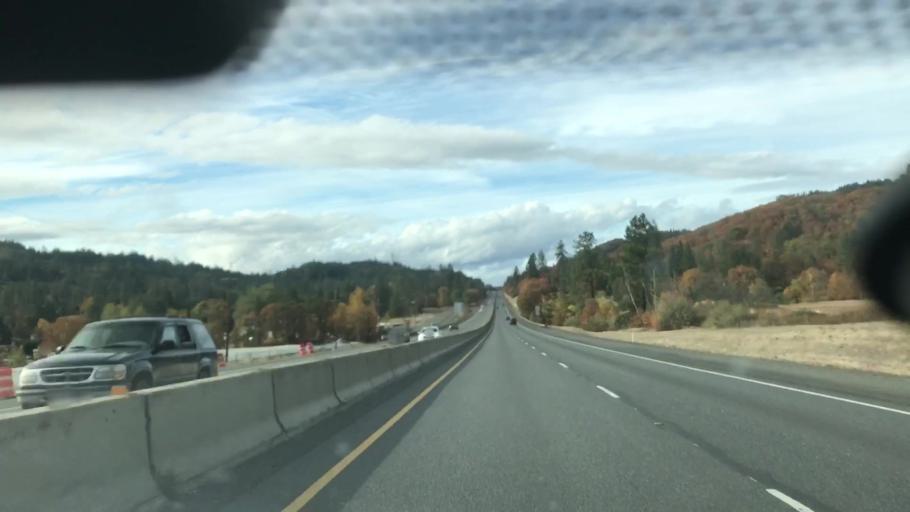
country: US
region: Oregon
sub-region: Josephine County
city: Grants Pass
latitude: 42.4674
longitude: -123.3290
